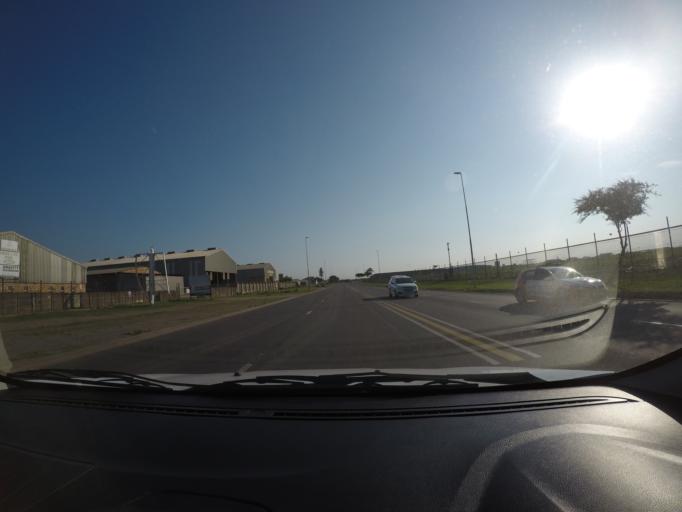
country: ZA
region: KwaZulu-Natal
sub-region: uThungulu District Municipality
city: Richards Bay
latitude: -28.7452
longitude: 32.0335
